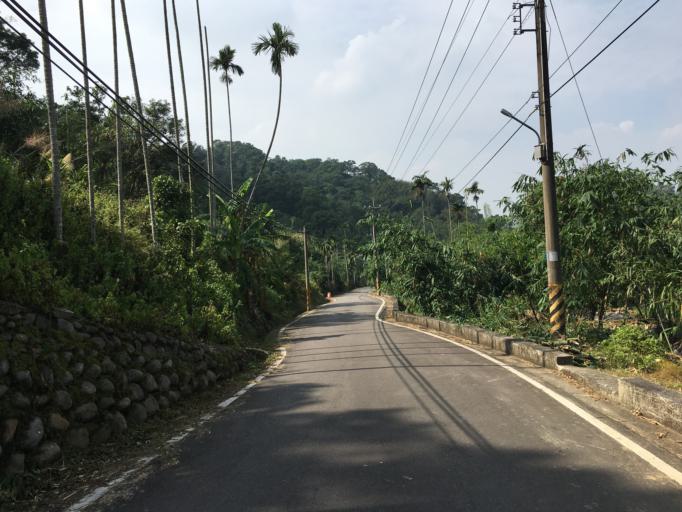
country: TW
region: Taiwan
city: Fengyuan
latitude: 24.1835
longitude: 120.7766
